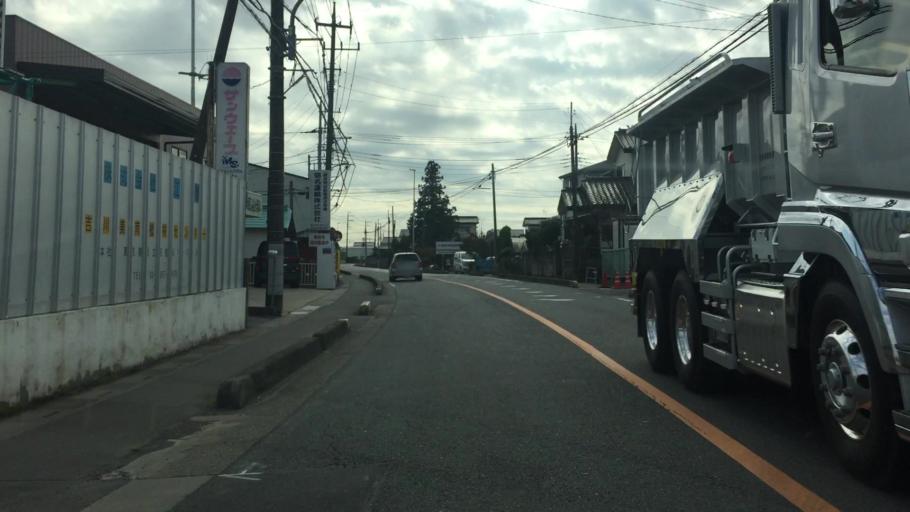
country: JP
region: Saitama
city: Yoshikawa
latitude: 35.8712
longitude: 139.8643
